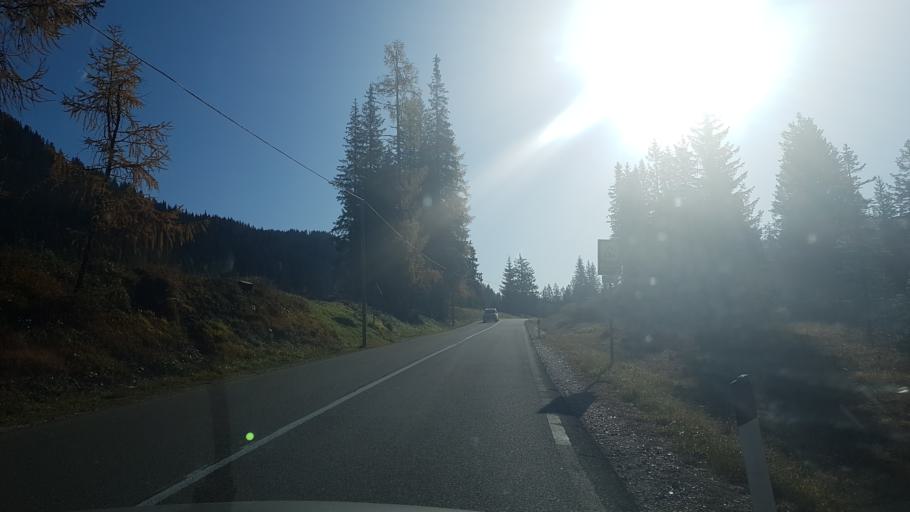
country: IT
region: Trentino-Alto Adige
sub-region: Bolzano
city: Sesto
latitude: 46.6690
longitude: 12.3972
